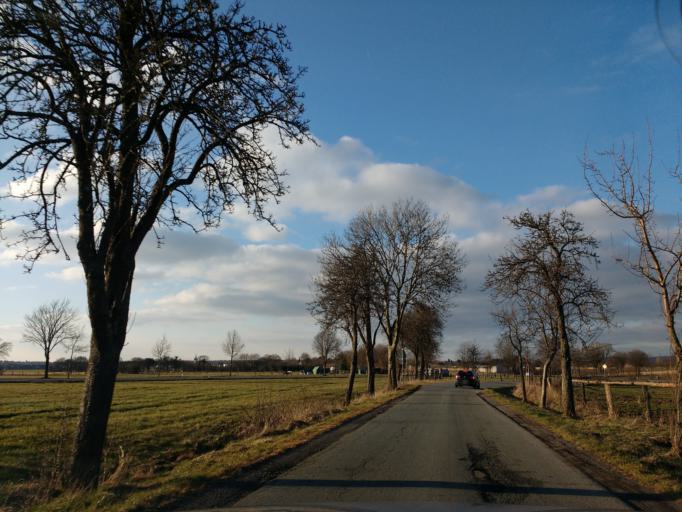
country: DE
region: North Rhine-Westphalia
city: Bad Lippspringe
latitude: 51.7681
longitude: 8.8384
